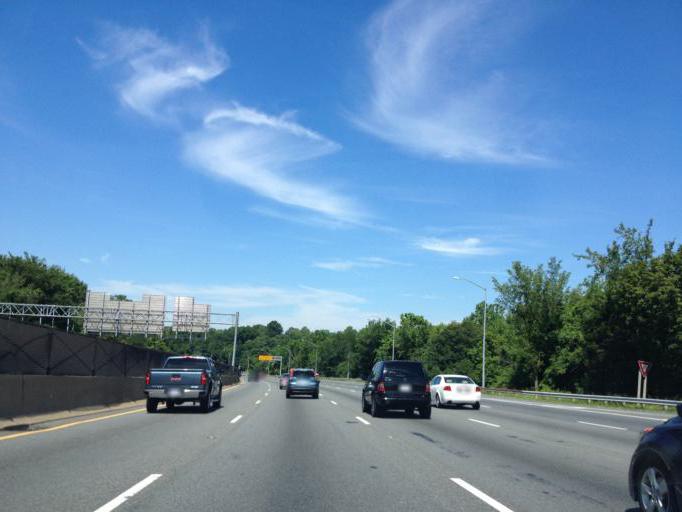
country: US
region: Maryland
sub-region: Montgomery County
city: Hillandale
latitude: 39.0196
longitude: -76.9788
